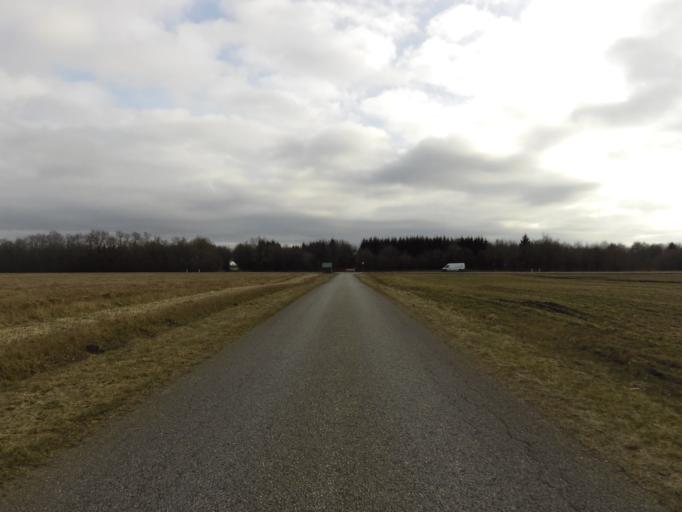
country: DK
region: South Denmark
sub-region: Tonder Kommune
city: Toftlund
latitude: 55.2018
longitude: 9.1814
